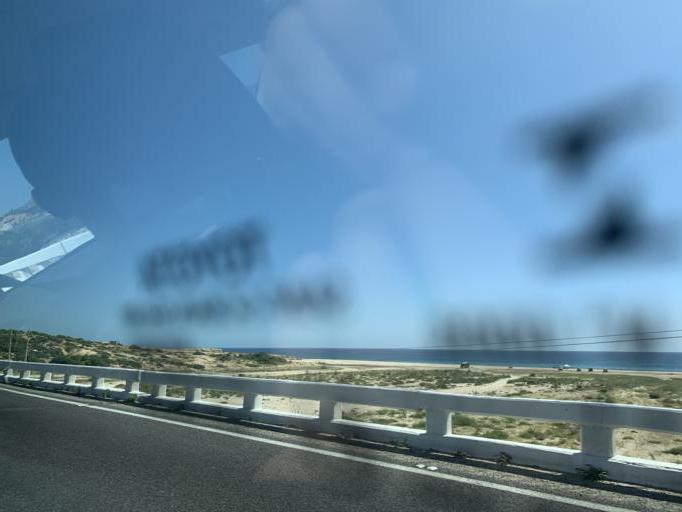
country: MX
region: Baja California Sur
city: Cabo San Lucas
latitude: 22.9617
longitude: -109.8019
